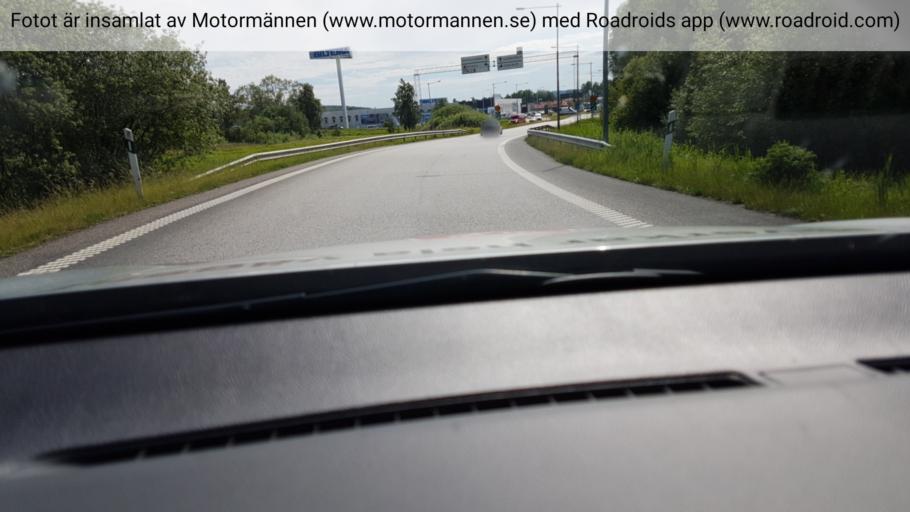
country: SE
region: Joenkoeping
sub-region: Jonkopings Kommun
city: Jonkoping
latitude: 57.7656
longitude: 14.1885
